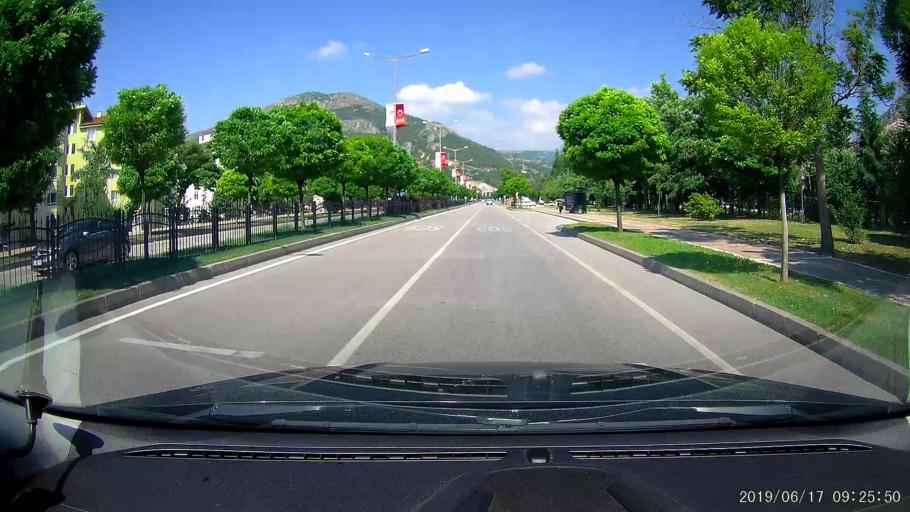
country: TR
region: Amasya
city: Amasya
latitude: 40.6683
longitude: 35.8434
